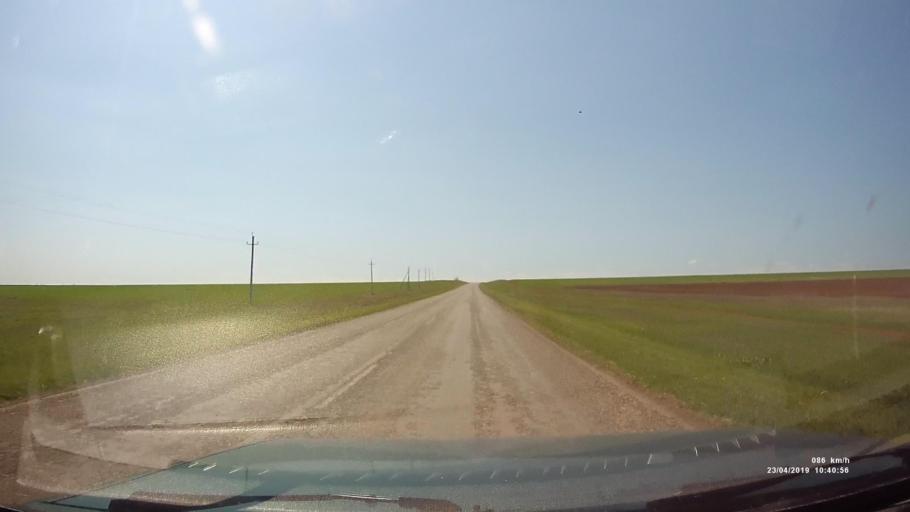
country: RU
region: Kalmykiya
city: Yashalta
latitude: 46.4999
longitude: 42.6384
